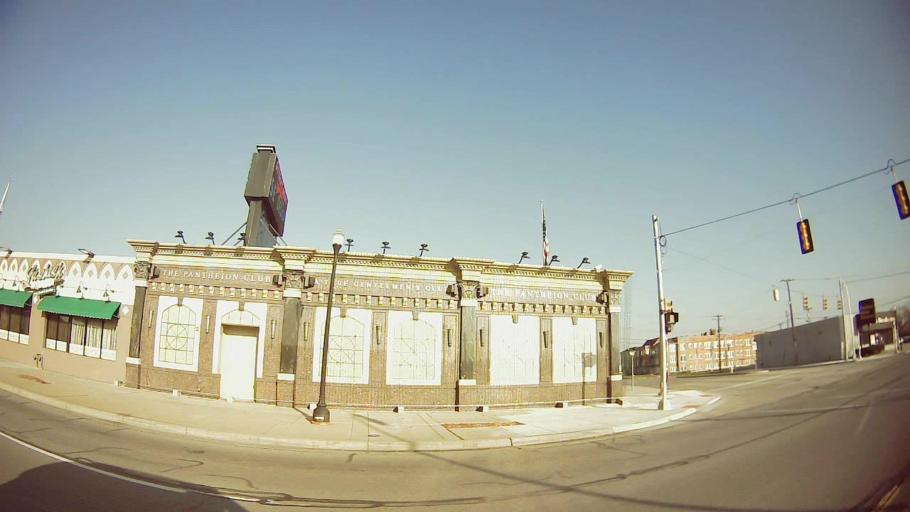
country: US
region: Michigan
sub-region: Wayne County
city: Dearborn
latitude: 42.3241
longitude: -83.1698
